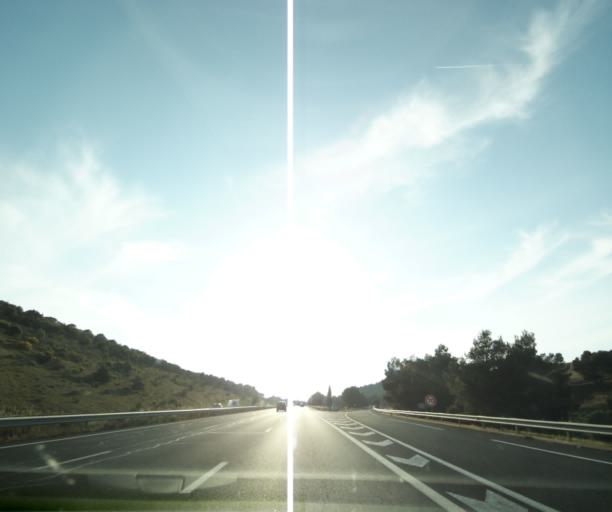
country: FR
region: Languedoc-Roussillon
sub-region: Departement de l'Aude
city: Narbonne
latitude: 43.1532
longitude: 2.9665
